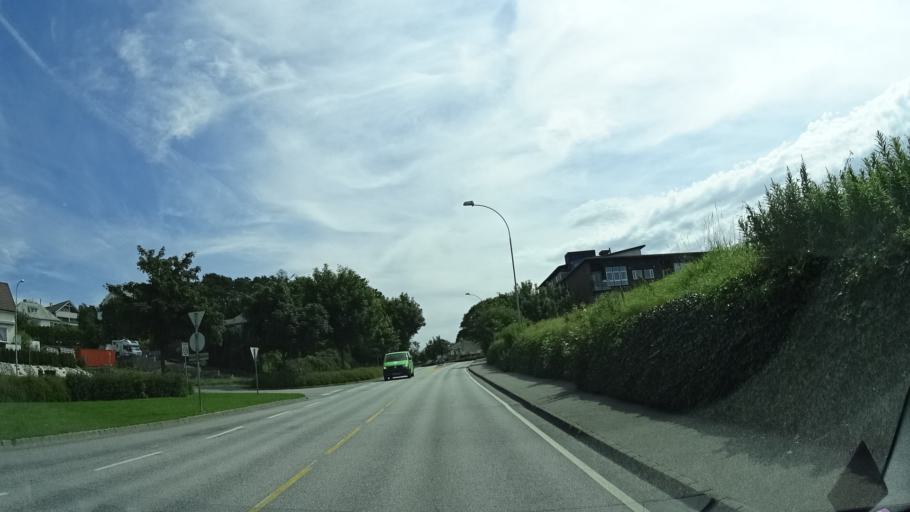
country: NO
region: Rogaland
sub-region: Stavanger
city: Stavanger
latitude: 58.9797
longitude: 5.6919
